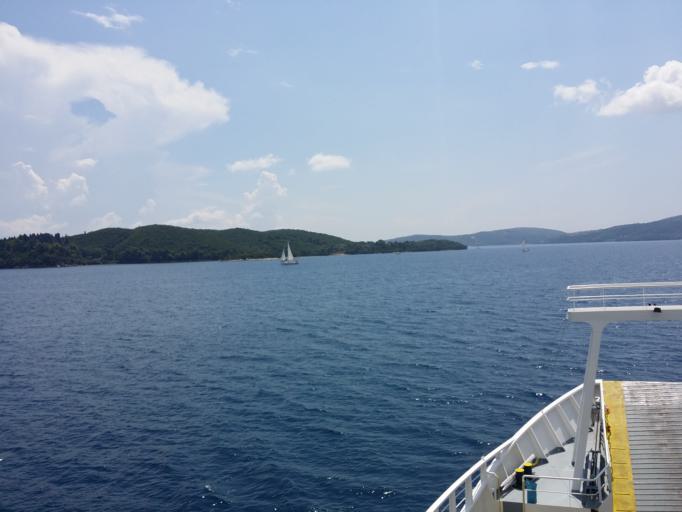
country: GR
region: Ionian Islands
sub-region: Lefkada
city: Nidri
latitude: 38.6963
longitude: 20.7275
